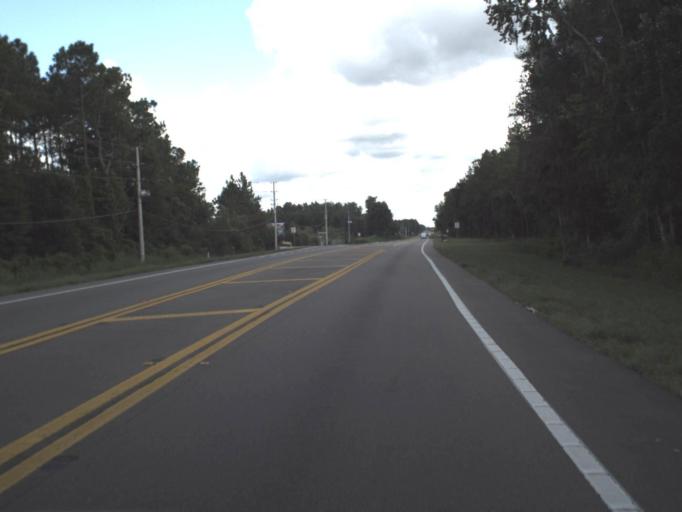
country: US
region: Florida
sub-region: Polk County
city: Kathleen
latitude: 28.1849
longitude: -81.9967
